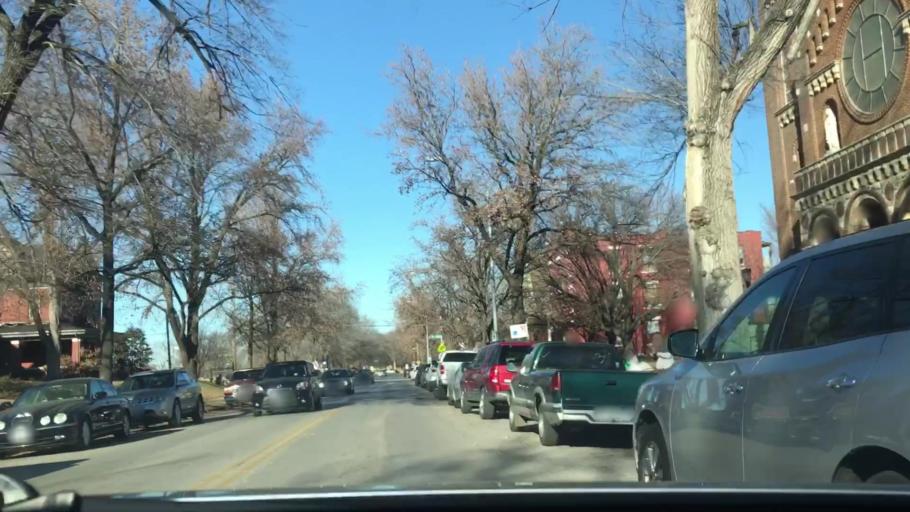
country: US
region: Missouri
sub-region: Clay County
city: North Kansas City
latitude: 39.1107
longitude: -94.5444
